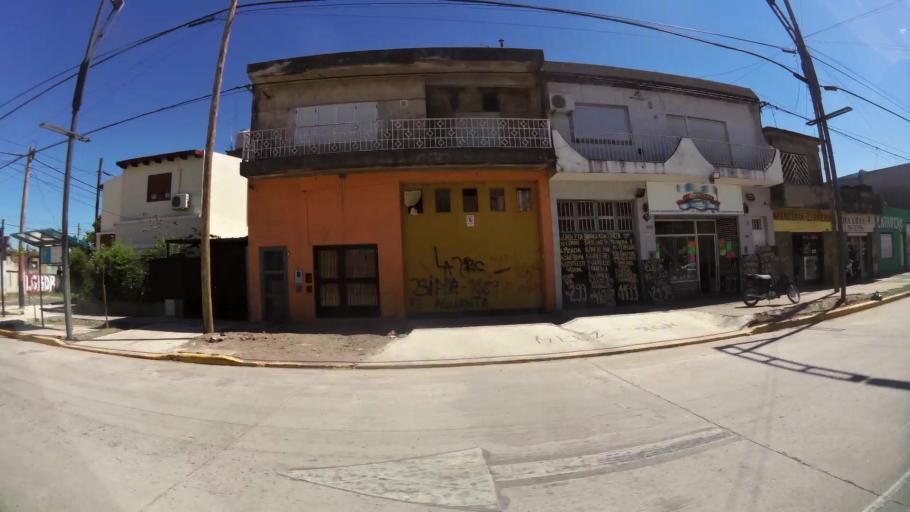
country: AR
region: Santa Fe
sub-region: Departamento de Rosario
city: Rosario
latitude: -32.9588
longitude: -60.6989
